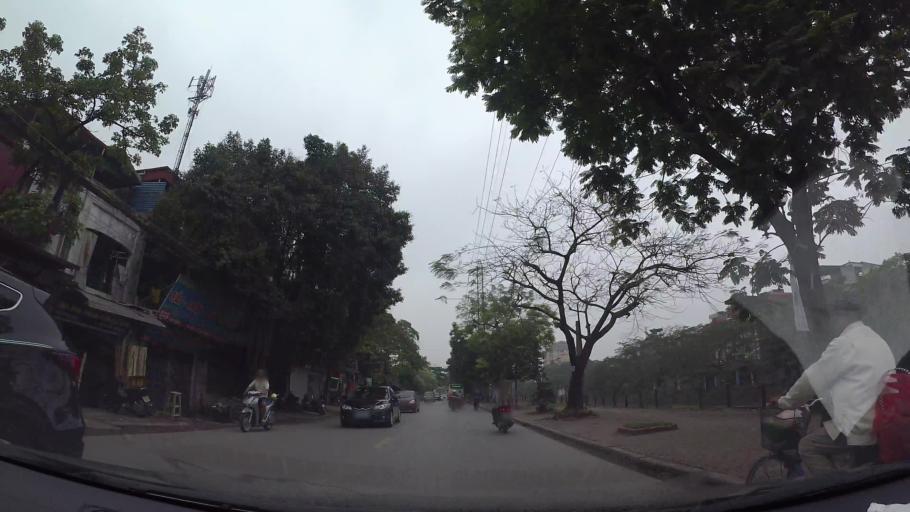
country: VN
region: Ha Noi
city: Hai BaTrung
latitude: 20.9867
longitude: 105.8635
